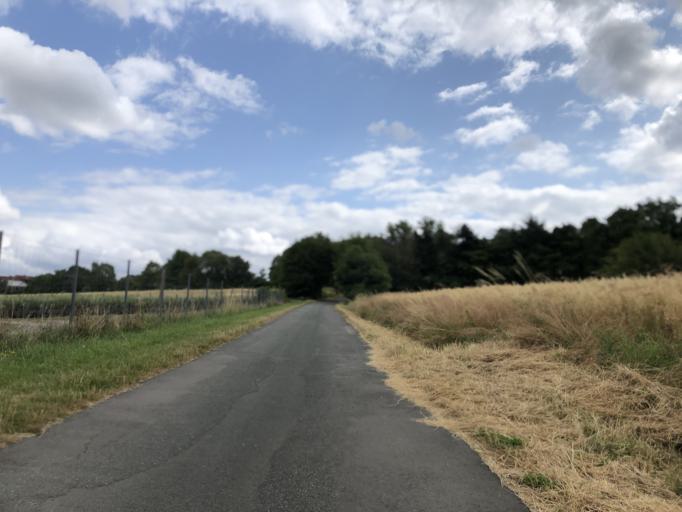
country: DE
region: North Rhine-Westphalia
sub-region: Regierungsbezirk Detmold
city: Detmold
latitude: 51.9370
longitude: 8.8414
